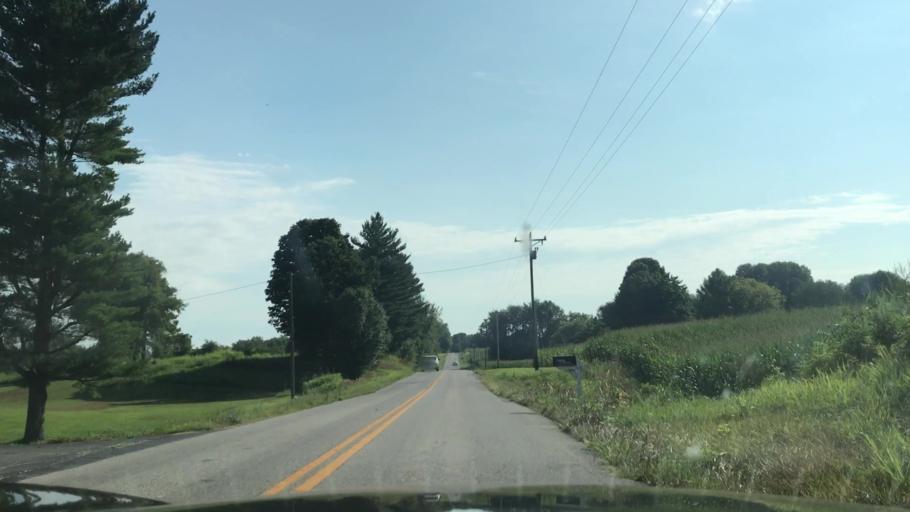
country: US
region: Kentucky
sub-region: Hart County
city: Horse Cave
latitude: 37.1830
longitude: -85.7752
